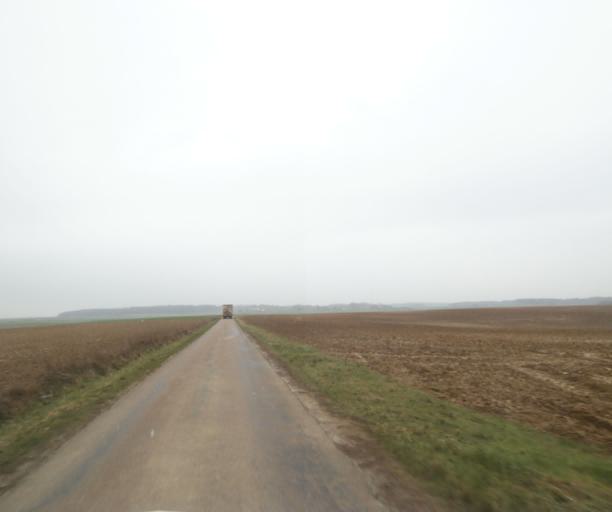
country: FR
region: Champagne-Ardenne
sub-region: Departement de la Haute-Marne
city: Chevillon
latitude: 48.5045
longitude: 5.0827
